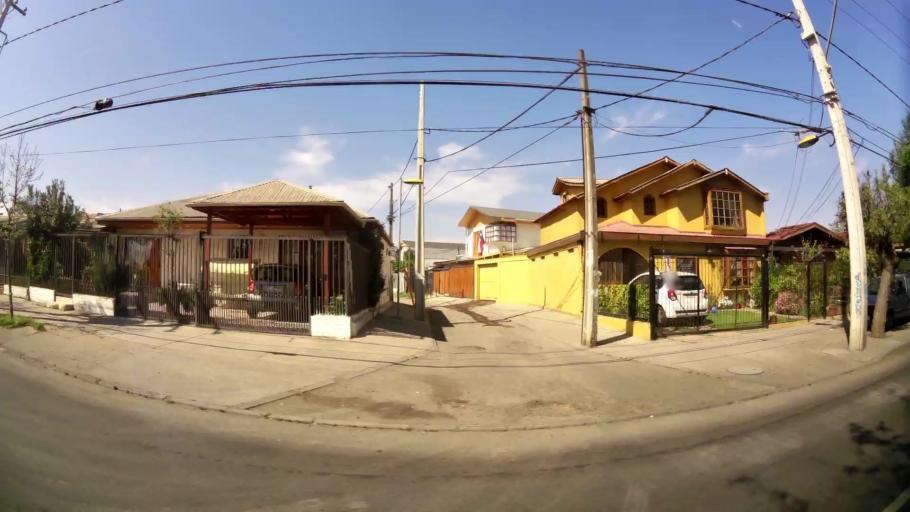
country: CL
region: Santiago Metropolitan
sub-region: Provincia de Santiago
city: Lo Prado
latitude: -33.4774
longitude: -70.7382
